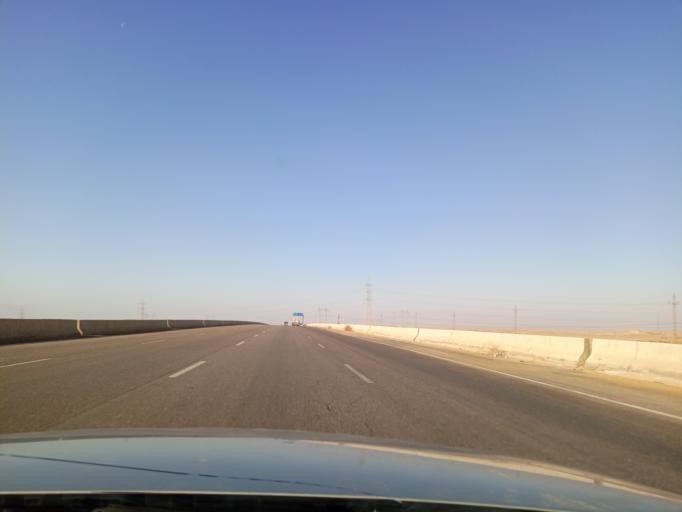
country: EG
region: Muhafazat al Fayyum
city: Tamiyah
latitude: 29.6328
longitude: 30.9747
